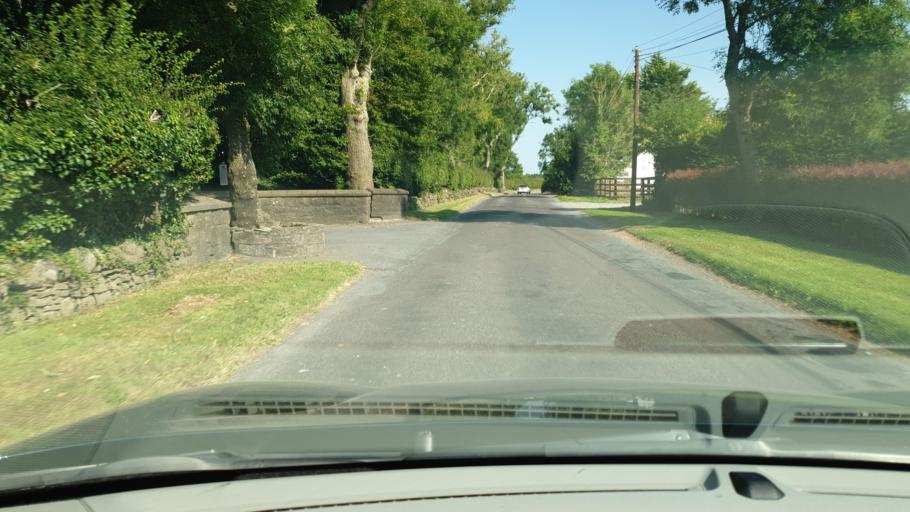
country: IE
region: Leinster
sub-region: An Mhi
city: Athboy
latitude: 53.6237
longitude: -6.9376
